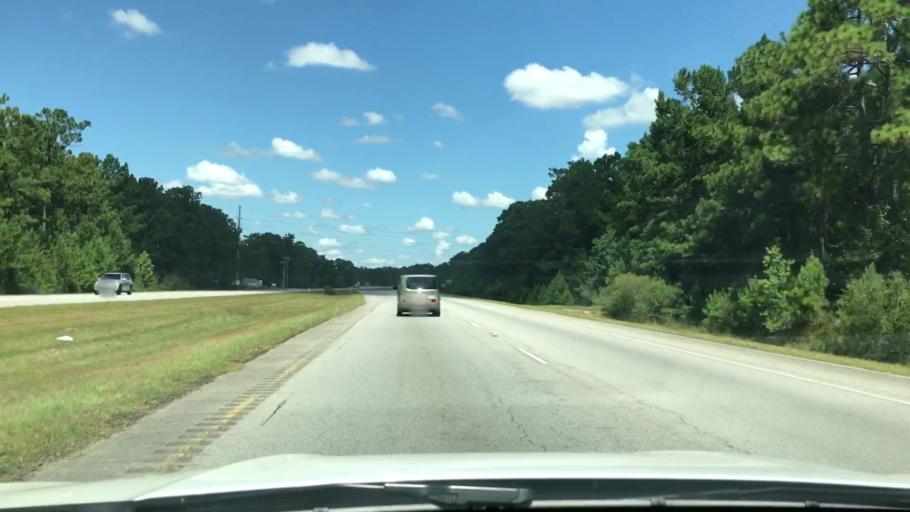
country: US
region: South Carolina
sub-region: Berkeley County
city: Hanahan
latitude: 32.9537
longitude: -80.0020
